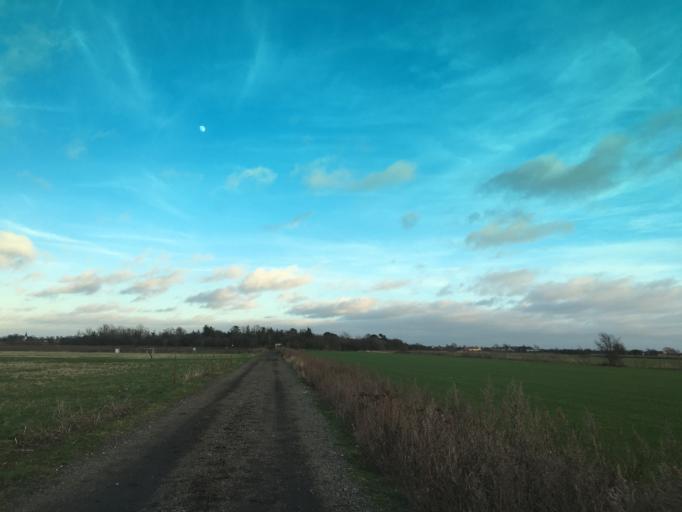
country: DK
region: Capital Region
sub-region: Tarnby Kommune
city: Tarnby
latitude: 55.5900
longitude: 12.6128
